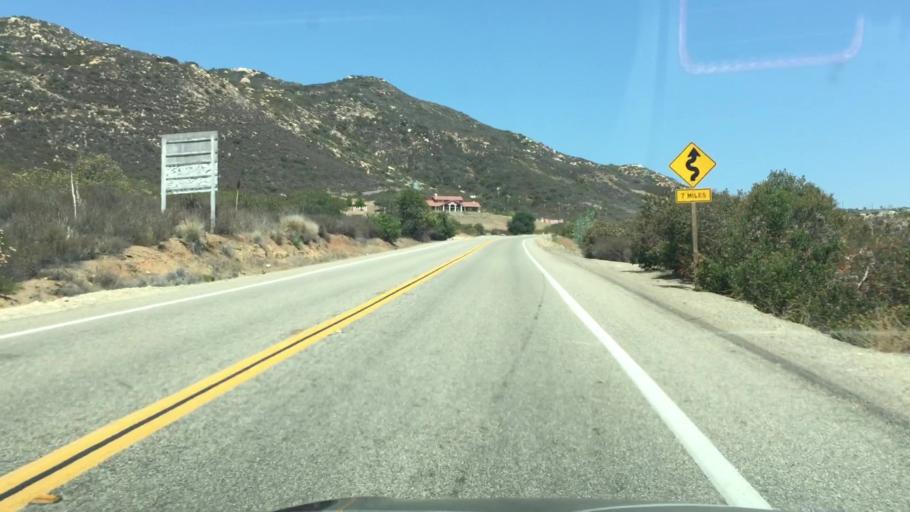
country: US
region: California
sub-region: San Diego County
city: Jamul
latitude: 32.7353
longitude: -116.8480
